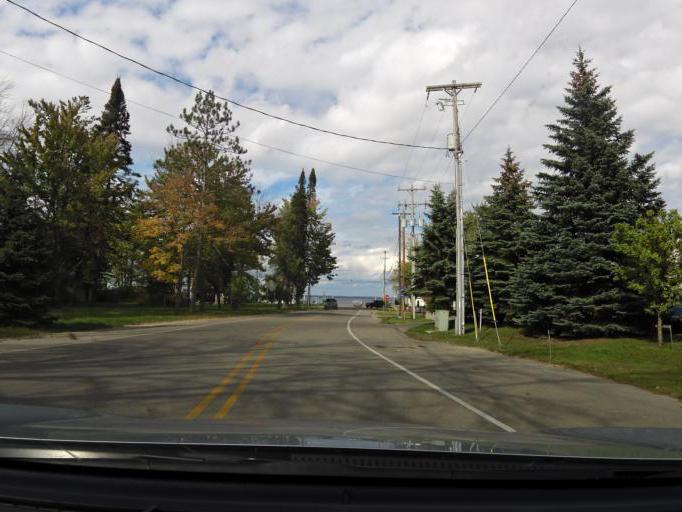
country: US
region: Michigan
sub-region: Roscommon County
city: Houghton Lake
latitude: 44.2988
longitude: -84.7124
